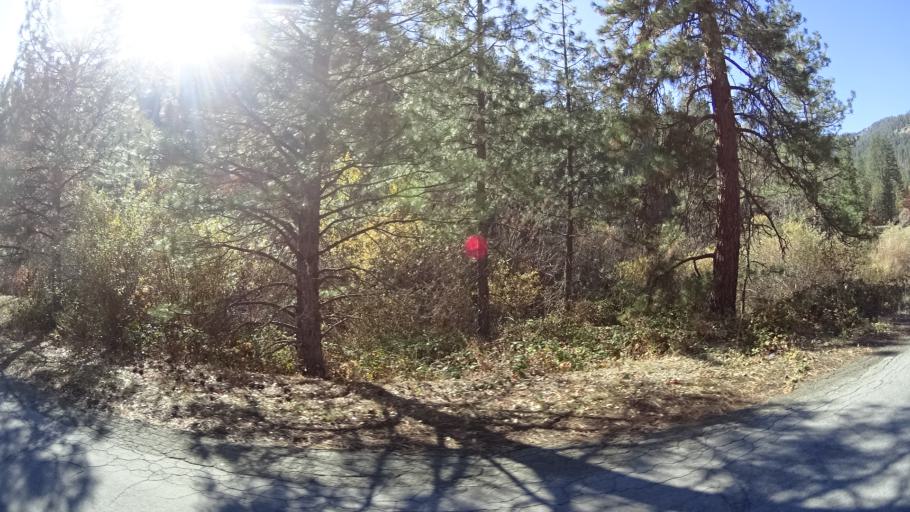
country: US
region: California
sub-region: Siskiyou County
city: Yreka
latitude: 41.7259
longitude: -122.7026
